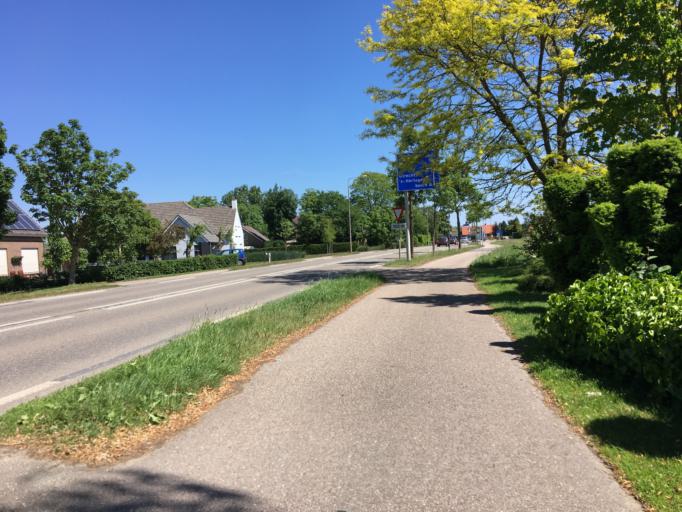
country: NL
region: Gelderland
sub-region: Gemeente Maasdriel
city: Hedel
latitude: 51.7478
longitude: 5.2481
